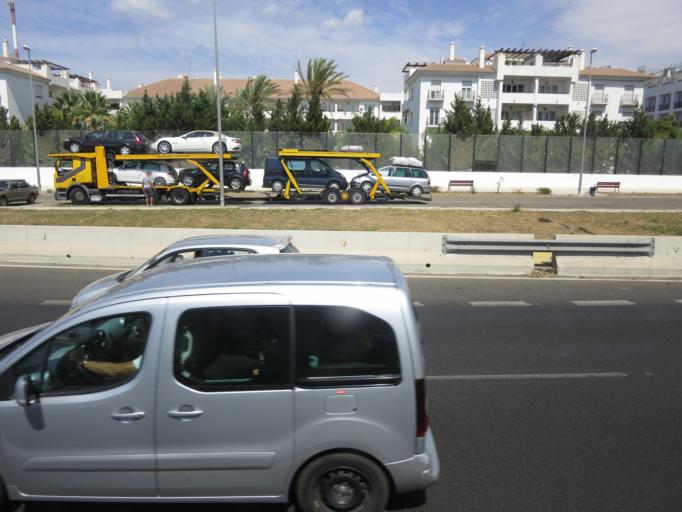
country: ES
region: Andalusia
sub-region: Provincia de Malaga
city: Benahavis
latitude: 36.4865
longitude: -4.9711
